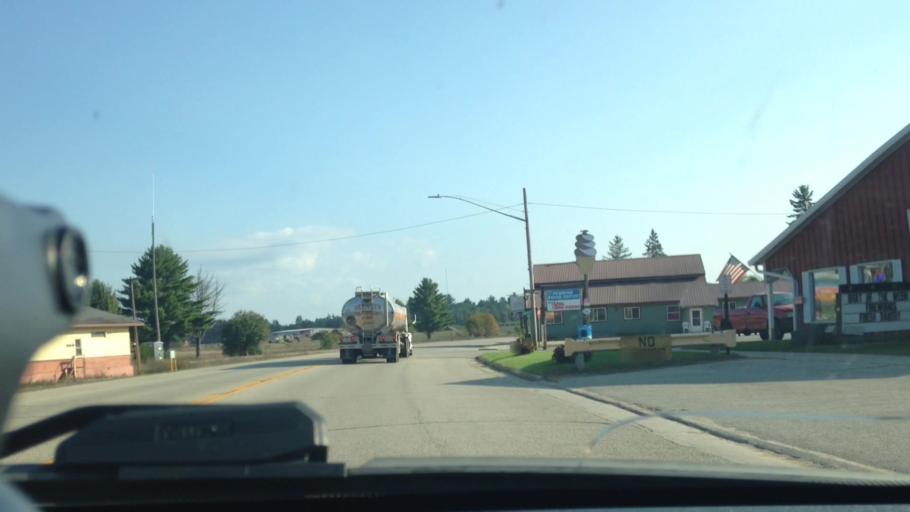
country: US
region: Wisconsin
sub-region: Marinette County
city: Niagara
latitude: 45.6345
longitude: -87.9911
